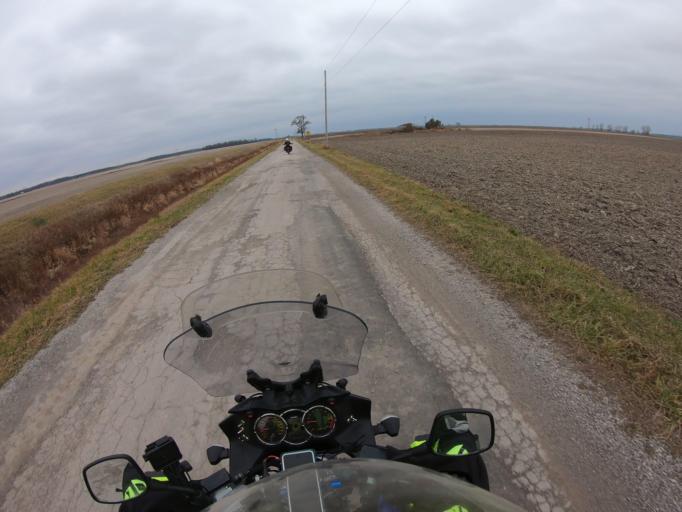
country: US
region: Michigan
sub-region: Saginaw County
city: Burt
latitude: 43.2637
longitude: -83.9731
